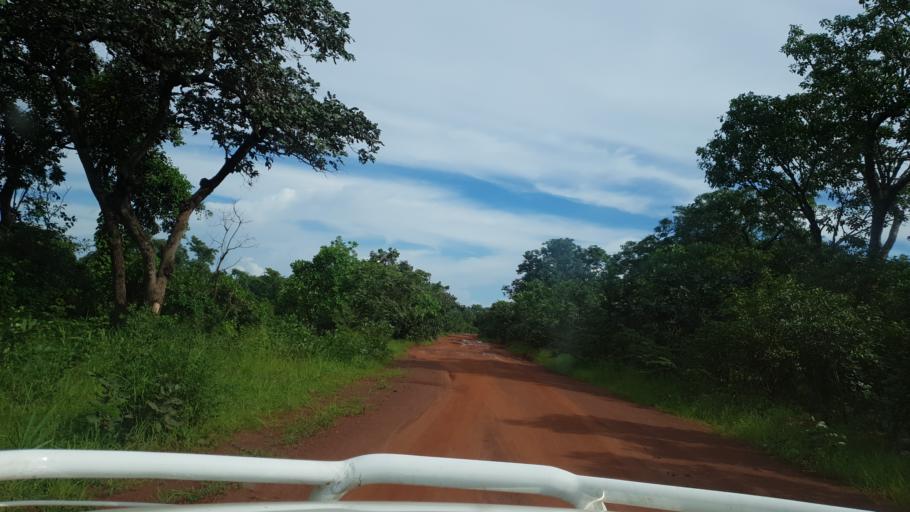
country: ML
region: Sikasso
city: Kolondieba
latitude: 10.7425
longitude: -6.9110
